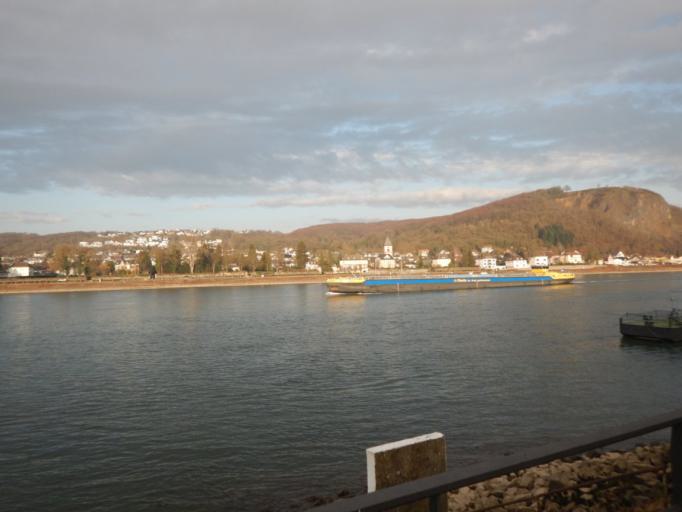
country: DE
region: Rheinland-Pfalz
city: Erpel
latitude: 50.5797
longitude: 7.2331
